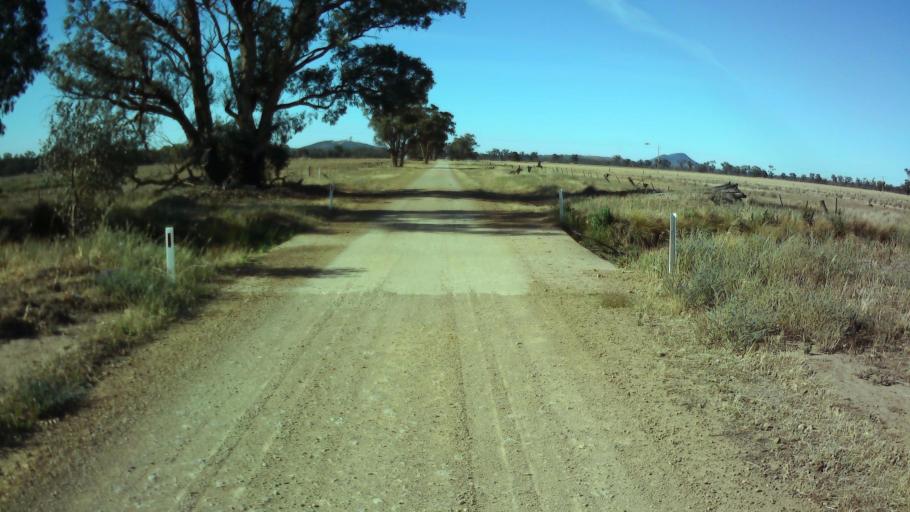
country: AU
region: New South Wales
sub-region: Weddin
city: Grenfell
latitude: -33.8461
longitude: 147.8763
